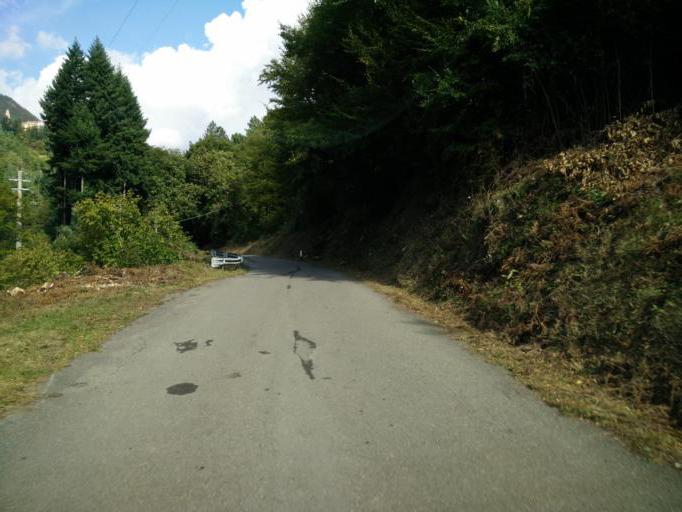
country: IT
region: Liguria
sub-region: Provincia di La Spezia
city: Sesta Godano
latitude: 44.3311
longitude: 9.6993
